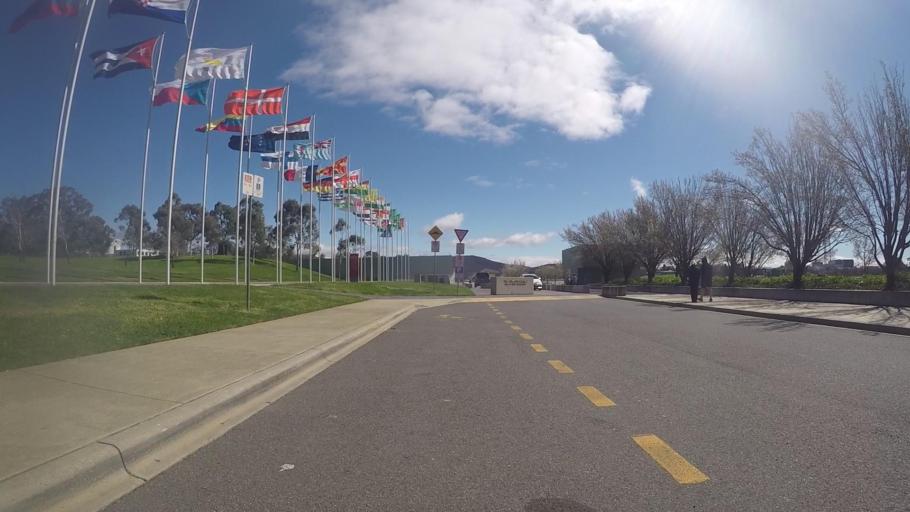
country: AU
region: Australian Capital Territory
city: Canberra
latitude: -35.2979
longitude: 149.1356
